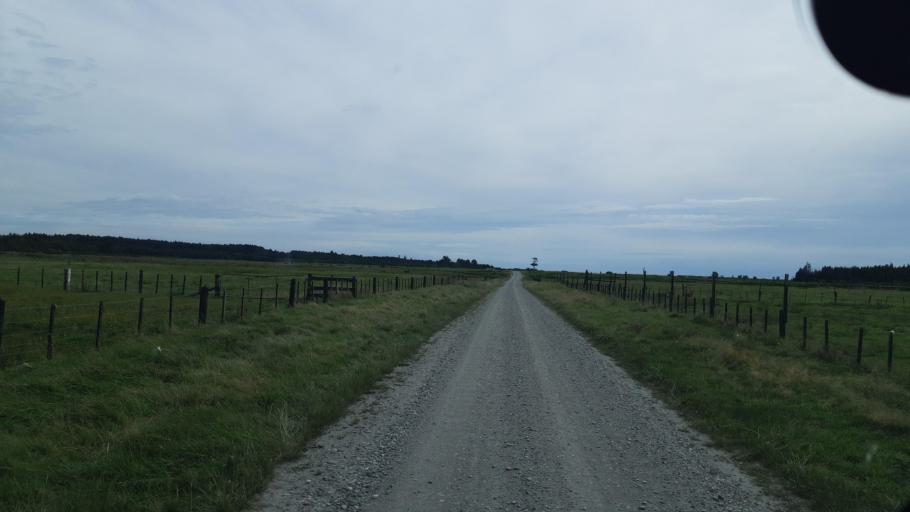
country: NZ
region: West Coast
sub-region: Westland District
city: Hokitika
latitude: -42.9728
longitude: 170.6775
